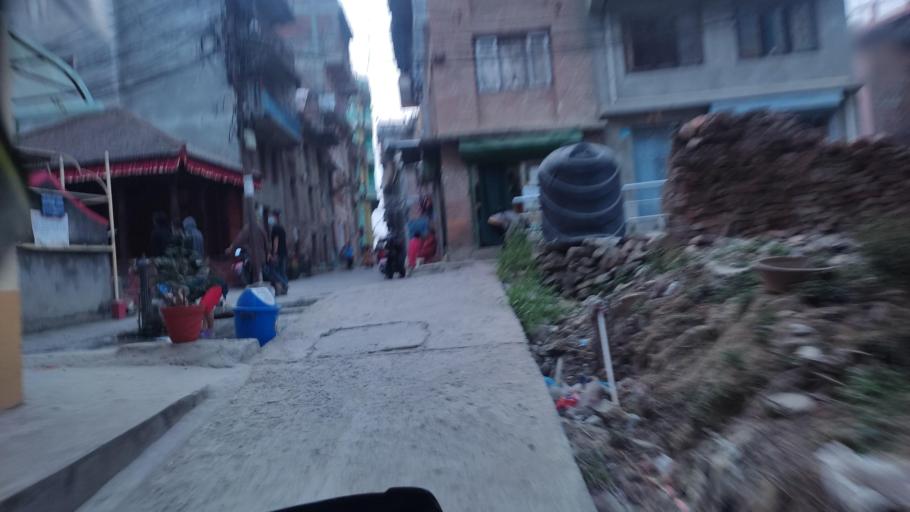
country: NP
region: Central Region
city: Kirtipur
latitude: 27.6688
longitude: 85.2770
